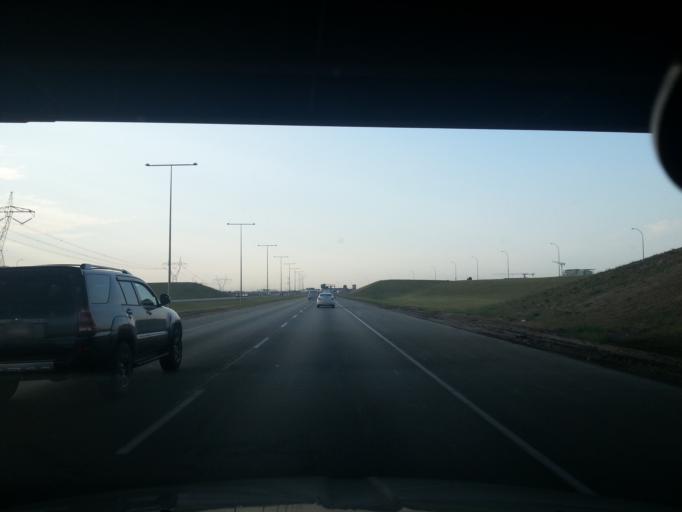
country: CA
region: Alberta
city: Devon
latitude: 53.4443
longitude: -113.6007
